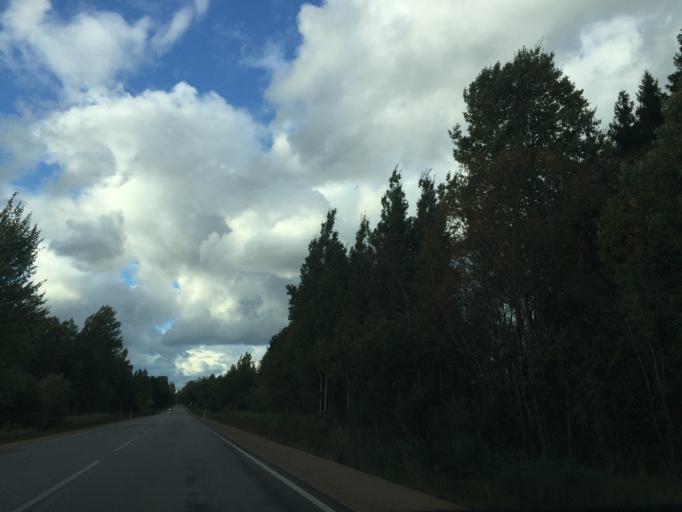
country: LV
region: Ligatne
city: Ligatne
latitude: 57.1735
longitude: 25.0423
